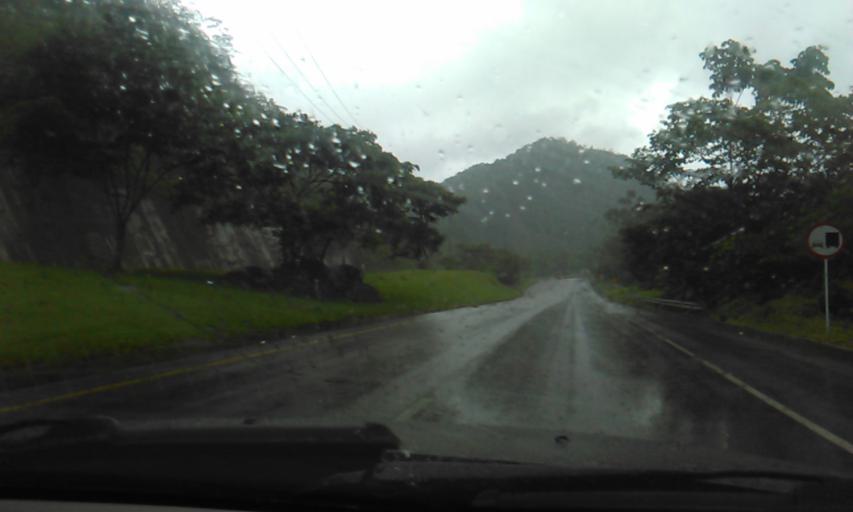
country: CO
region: Valle del Cauca
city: Buenaventura
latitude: 3.8619
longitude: -76.8313
